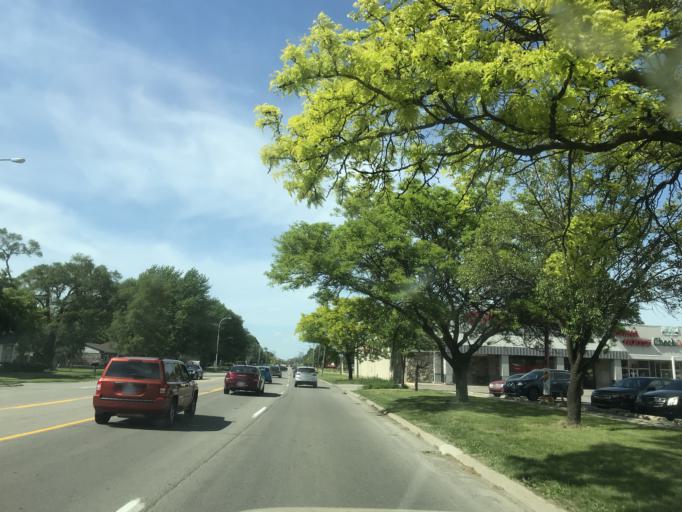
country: US
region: Michigan
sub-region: Wayne County
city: Redford
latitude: 42.3714
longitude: -83.3135
